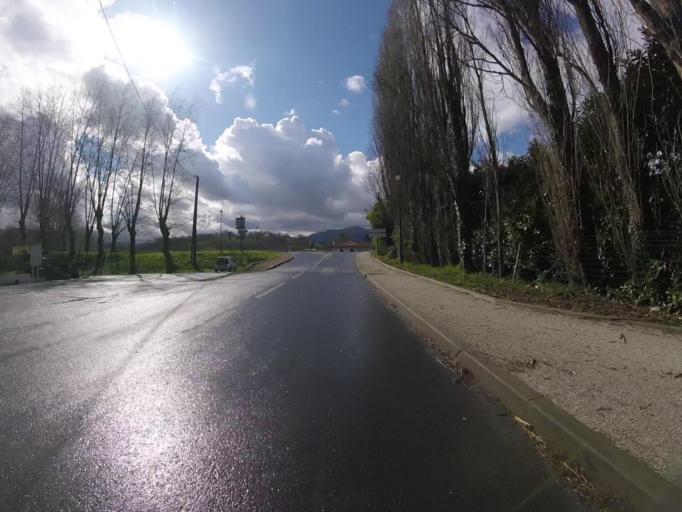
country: FR
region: Aquitaine
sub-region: Departement des Pyrenees-Atlantiques
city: Sare
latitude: 43.3101
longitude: -1.5723
